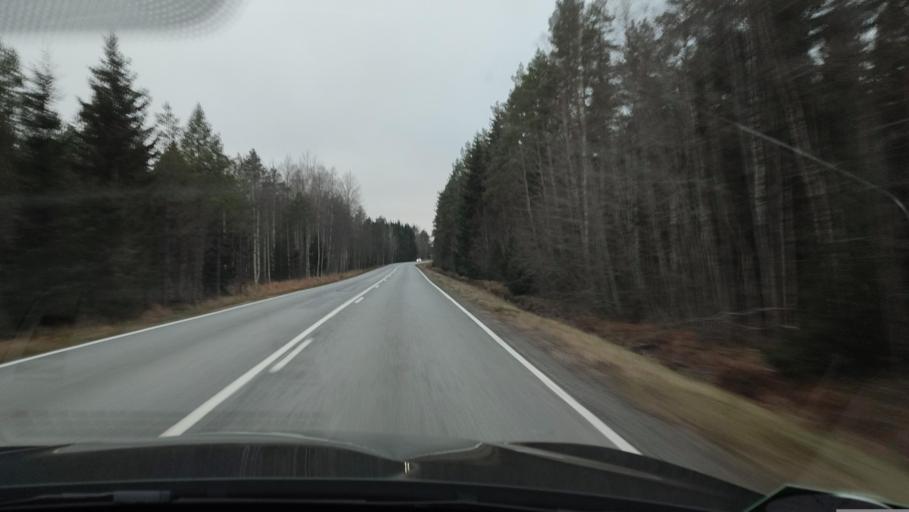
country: FI
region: Southern Ostrobothnia
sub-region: Suupohja
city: Karijoki
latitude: 62.3235
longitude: 21.8771
